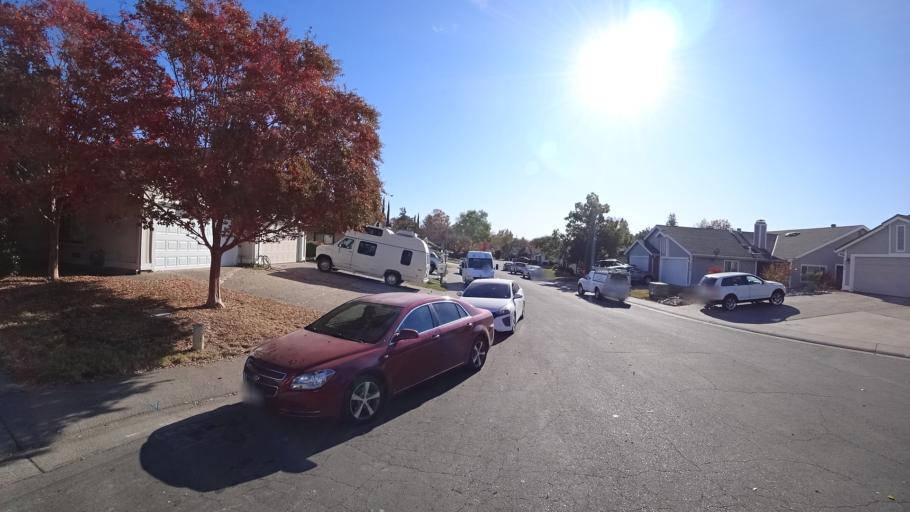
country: US
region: California
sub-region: Sacramento County
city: Citrus Heights
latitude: 38.6749
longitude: -121.2972
